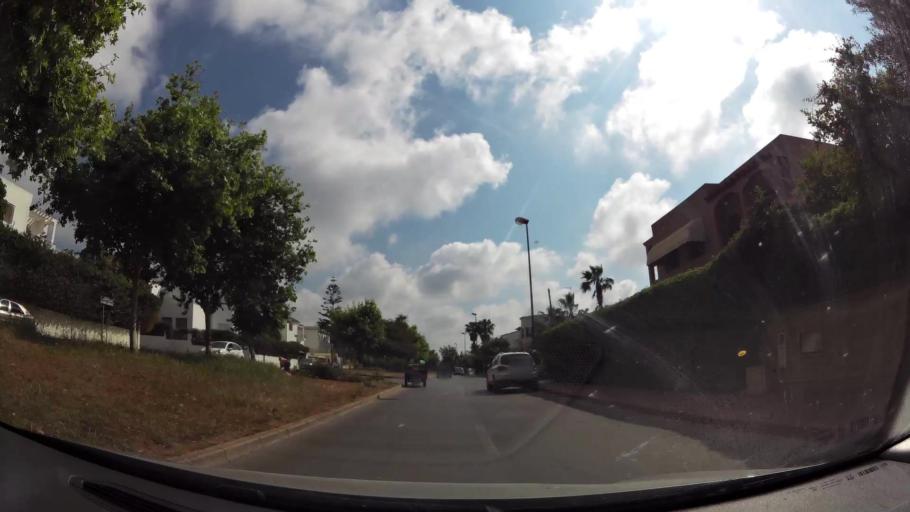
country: MA
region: Rabat-Sale-Zemmour-Zaer
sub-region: Skhirate-Temara
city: Temara
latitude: 33.9530
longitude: -6.8671
